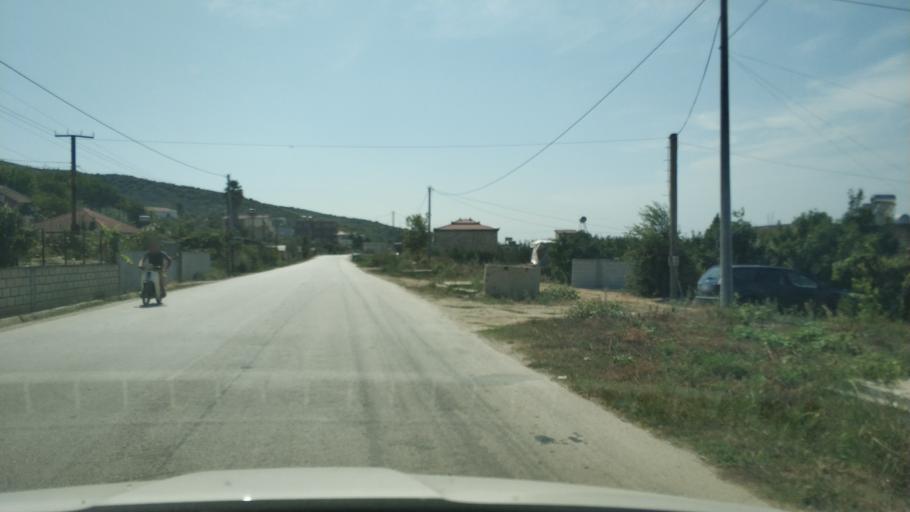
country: AL
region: Fier
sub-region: Rrethi i Lushnjes
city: Grabjan
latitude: 40.9428
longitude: 19.5375
